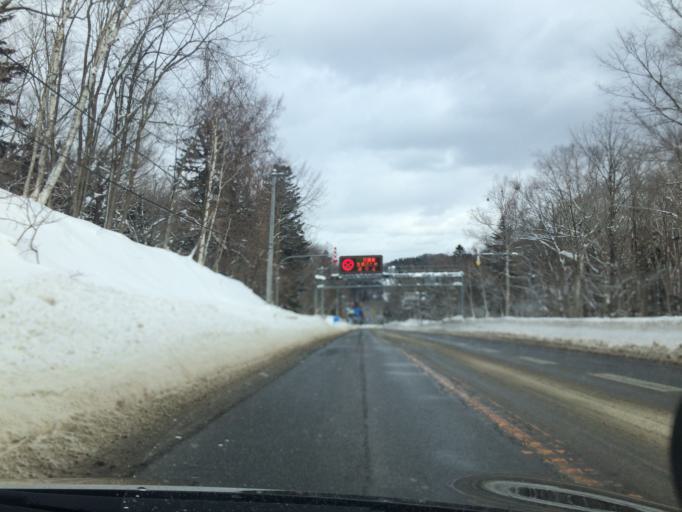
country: JP
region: Hokkaido
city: Shimo-furano
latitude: 42.9075
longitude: 142.3647
